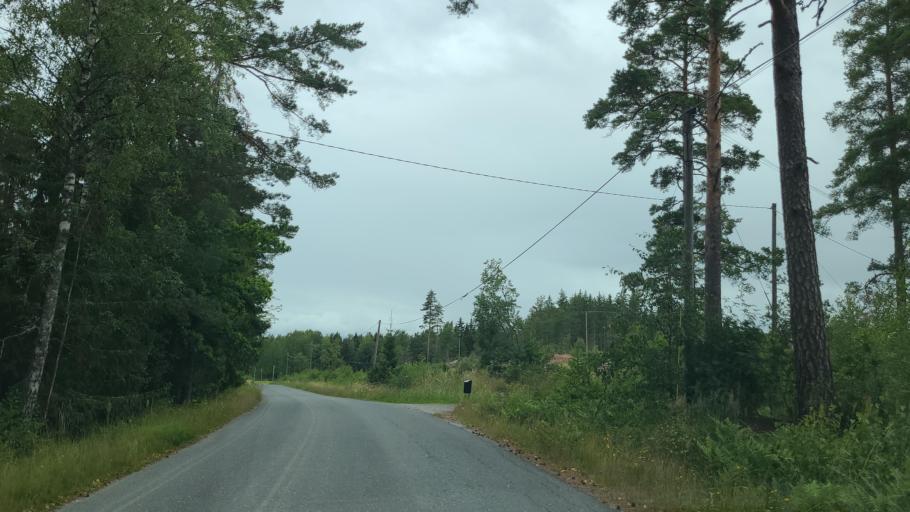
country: FI
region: Varsinais-Suomi
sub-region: Aboland-Turunmaa
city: Dragsfjaerd
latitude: 60.0761
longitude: 22.4489
